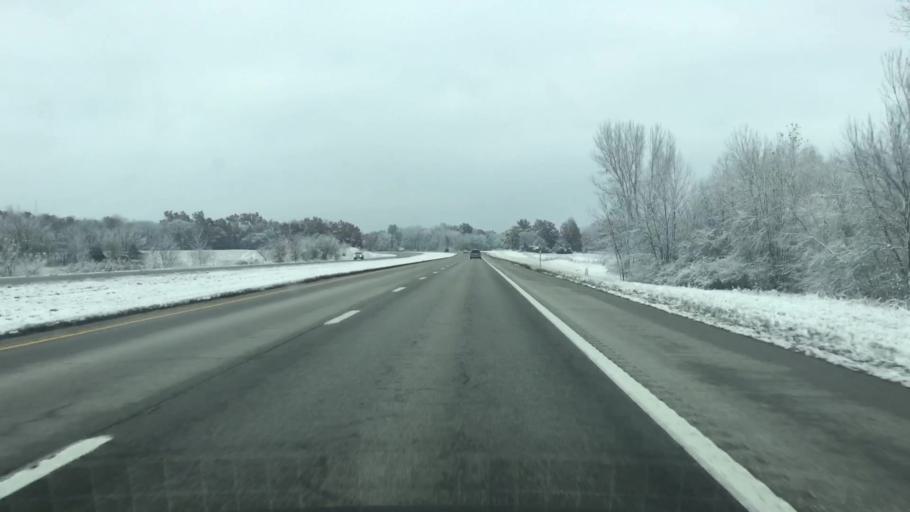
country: US
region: Missouri
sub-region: Cass County
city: Garden City
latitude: 38.5099
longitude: -94.0994
